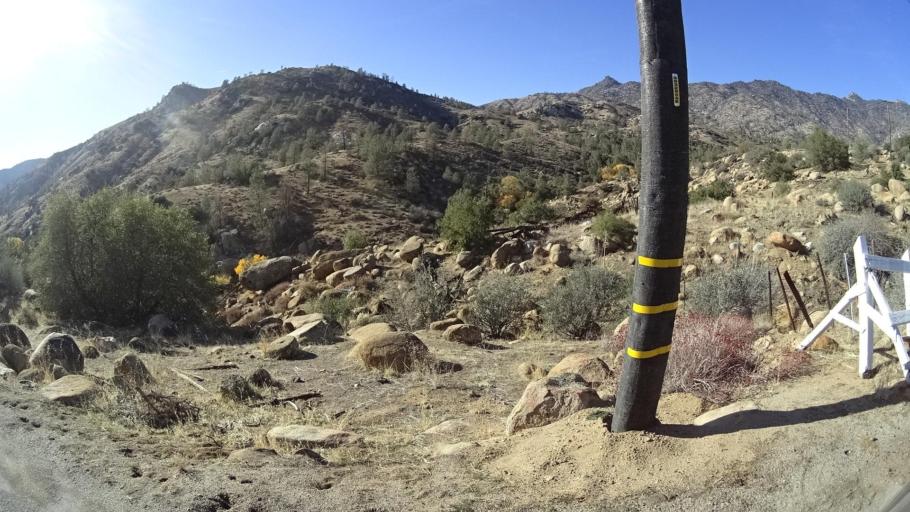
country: US
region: California
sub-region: Kern County
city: Weldon
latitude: 35.7251
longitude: -118.3041
